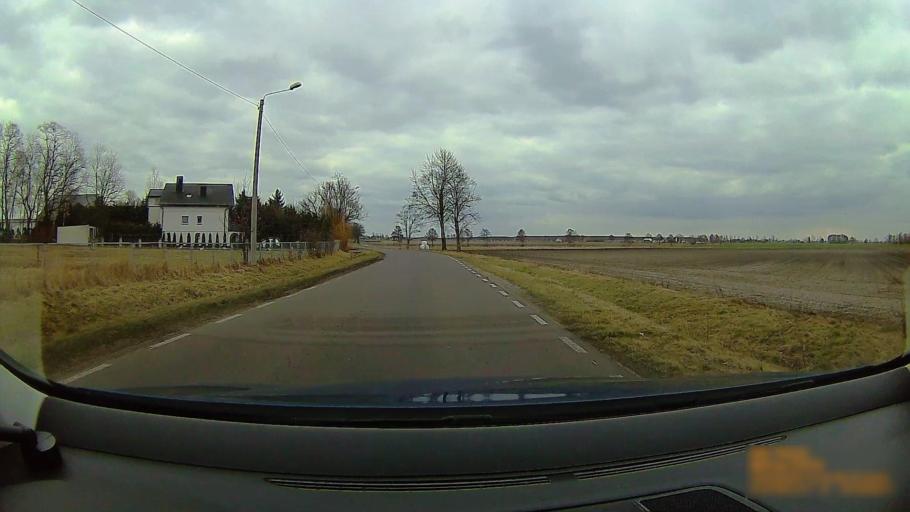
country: PL
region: Greater Poland Voivodeship
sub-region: Powiat koninski
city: Rzgow Pierwszy
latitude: 52.1007
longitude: 18.0992
